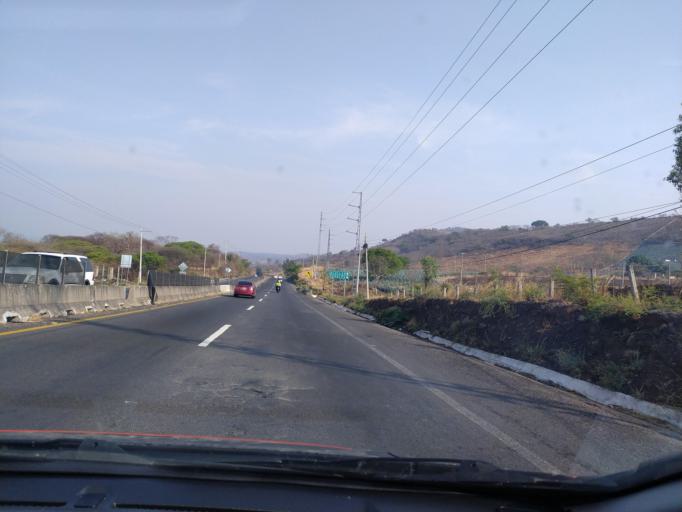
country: MX
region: Jalisco
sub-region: Acatlan de Juarez
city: Villa de los Ninos
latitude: 20.4298
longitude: -103.5660
